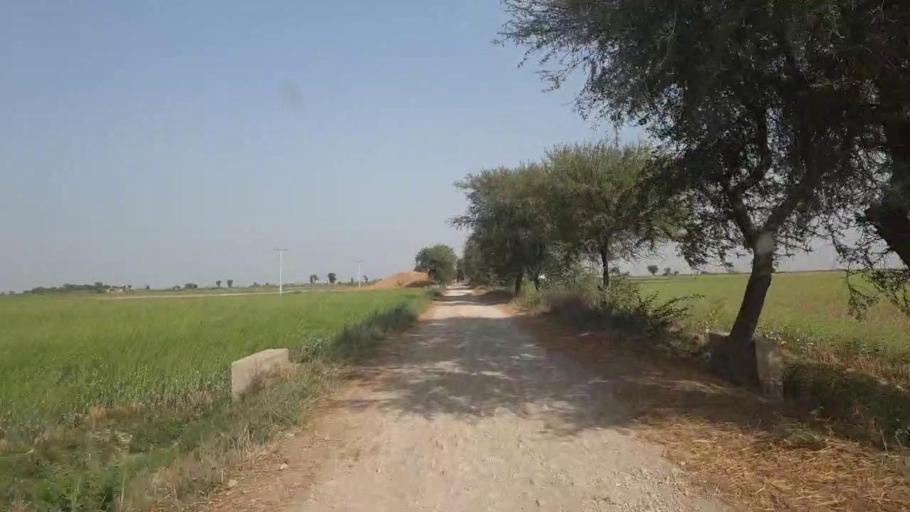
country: PK
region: Sindh
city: Kario
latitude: 24.5531
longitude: 68.5386
